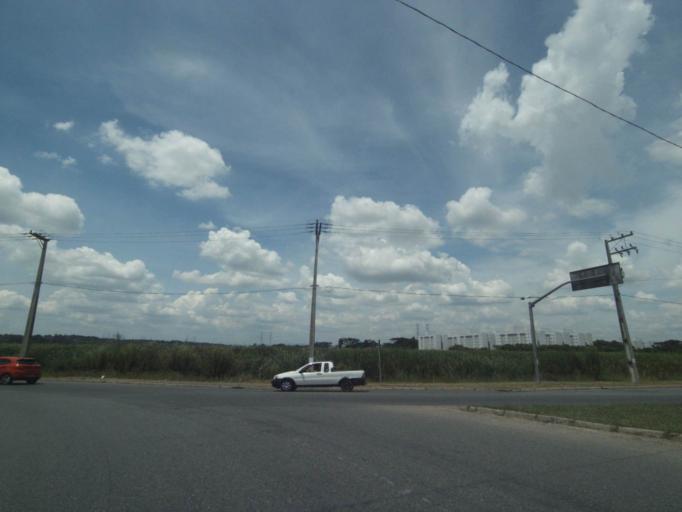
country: BR
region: Parana
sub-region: Sao Jose Dos Pinhais
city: Sao Jose dos Pinhais
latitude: -25.4967
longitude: -49.1635
